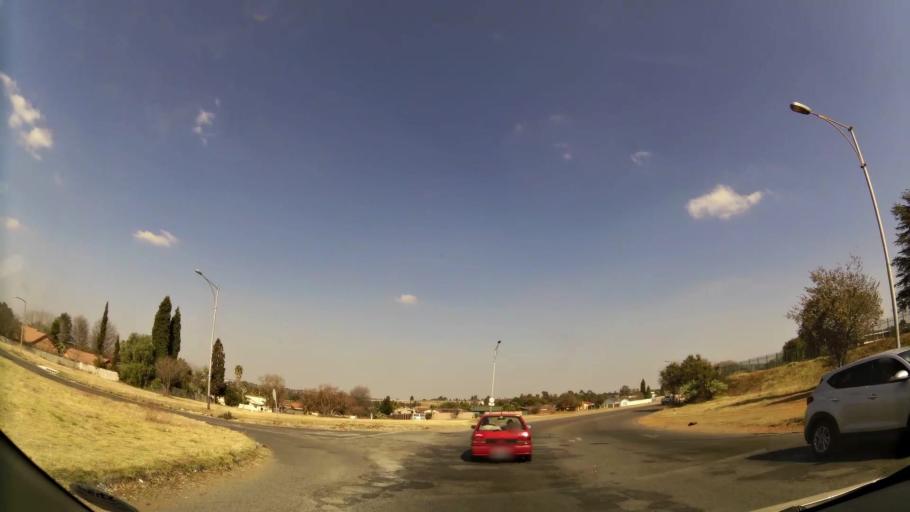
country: ZA
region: Gauteng
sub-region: West Rand District Municipality
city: Krugersdorp
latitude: -26.1222
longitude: 27.8172
